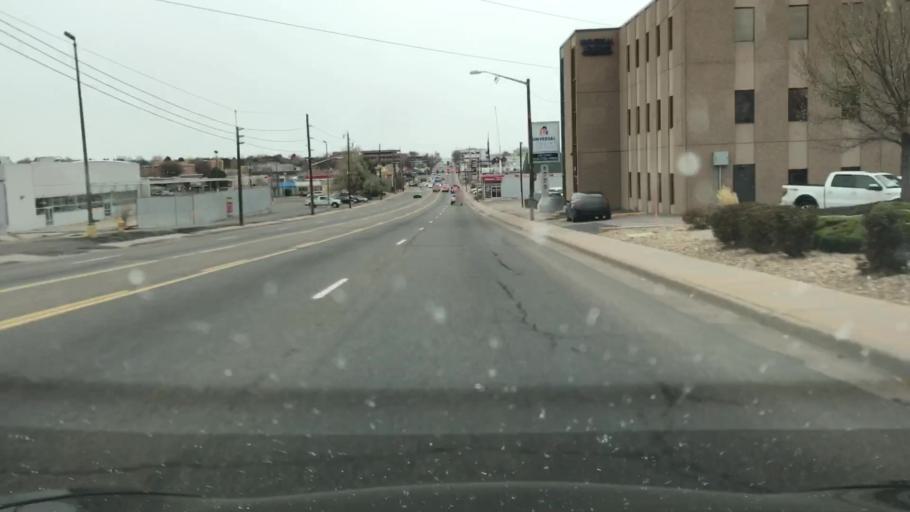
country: US
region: Colorado
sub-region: Arapahoe County
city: Glendale
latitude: 39.6785
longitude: -104.9090
